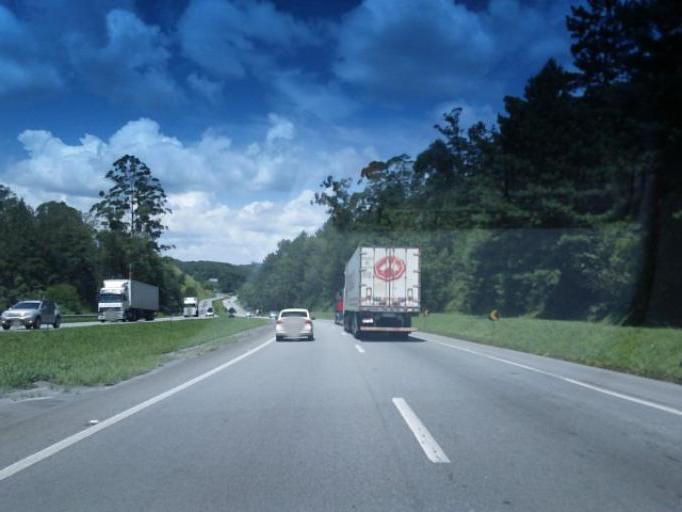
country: BR
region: Sao Paulo
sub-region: Juquitiba
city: Juquitiba
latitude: -23.9385
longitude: -47.0864
